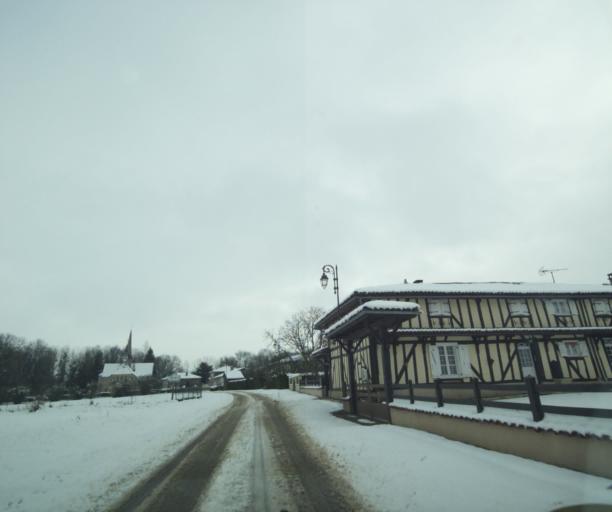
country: FR
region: Champagne-Ardenne
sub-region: Departement de la Haute-Marne
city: Montier-en-Der
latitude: 48.4964
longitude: 4.6987
